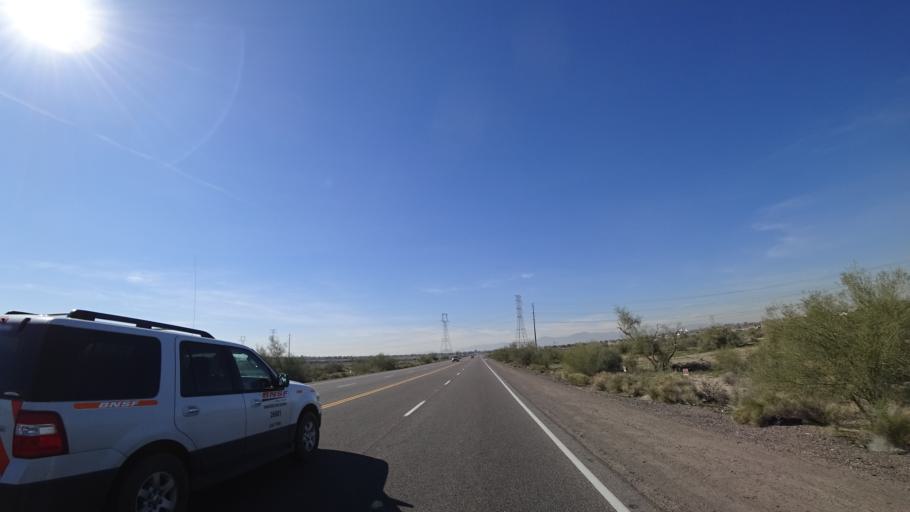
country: US
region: Arizona
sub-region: Maricopa County
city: Litchfield Park
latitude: 33.5076
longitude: -112.3113
